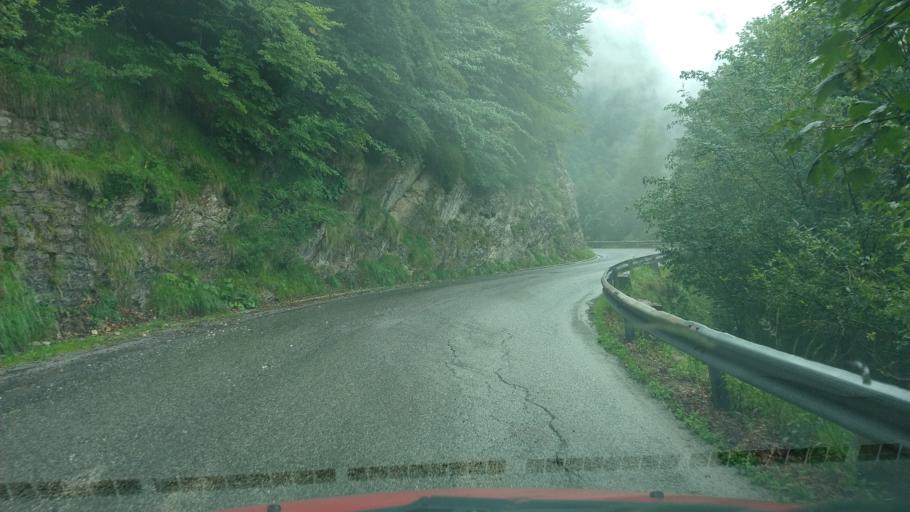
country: IT
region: Veneto
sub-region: Provincia di Vicenza
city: Tonezza del Cimone
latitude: 45.8758
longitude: 11.3273
